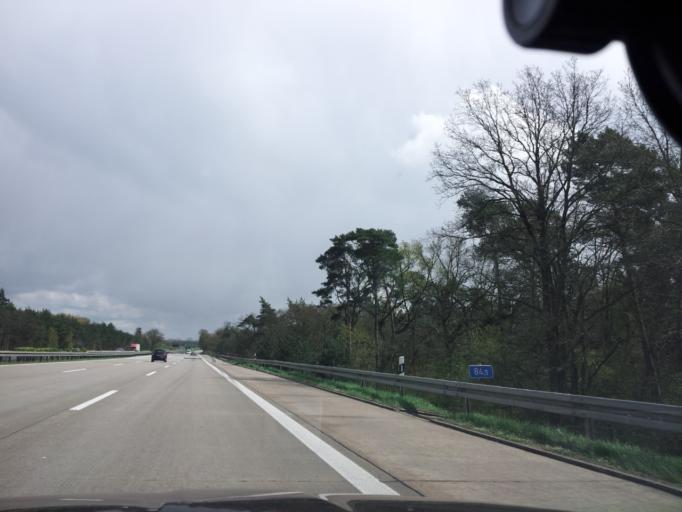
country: DE
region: Brandenburg
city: Michendorf
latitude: 52.3026
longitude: 13.1148
